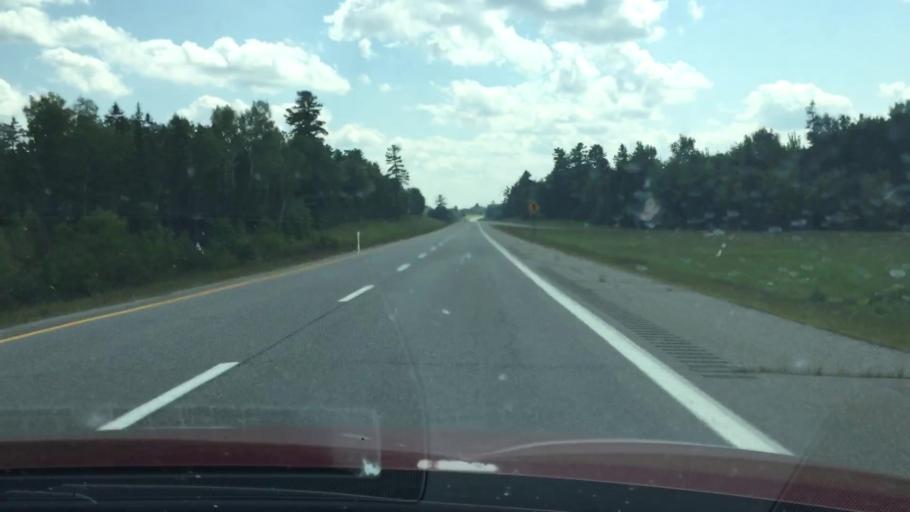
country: US
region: Maine
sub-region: Penobscot County
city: Lincoln
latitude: 45.3744
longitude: -68.6057
